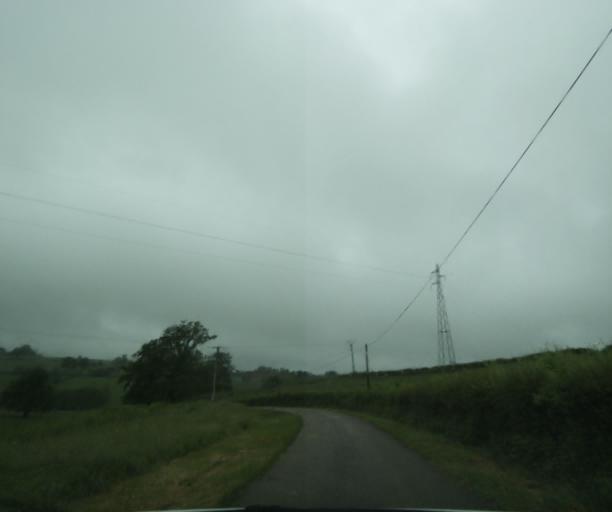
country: FR
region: Bourgogne
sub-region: Departement de Saone-et-Loire
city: Charolles
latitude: 46.4623
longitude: 4.2185
